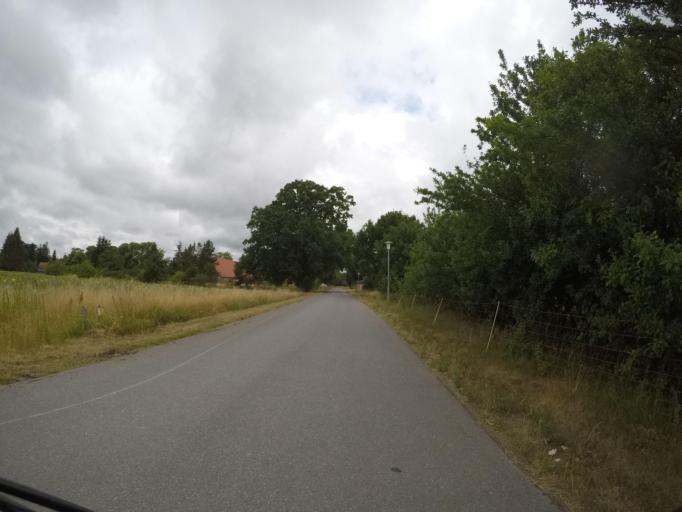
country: DE
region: Lower Saxony
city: Hitzacker
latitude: 53.1816
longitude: 11.1095
